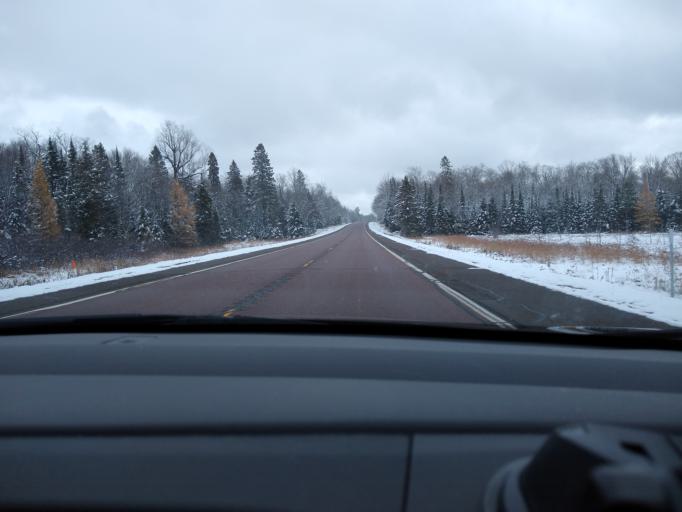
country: US
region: Michigan
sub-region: Iron County
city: Iron River
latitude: 46.1814
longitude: -88.9636
